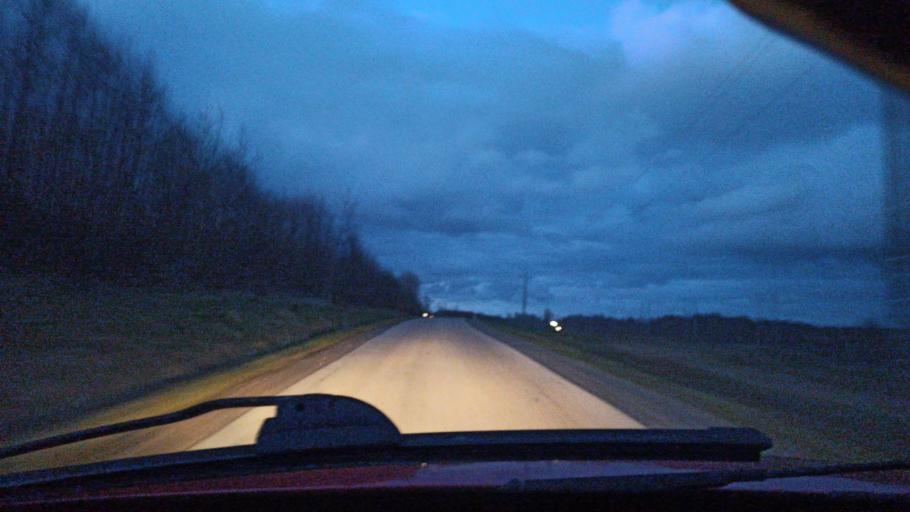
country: PL
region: Warmian-Masurian Voivodeship
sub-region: Powiat elblaski
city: Gronowo Gorne
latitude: 54.1745
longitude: 19.5376
